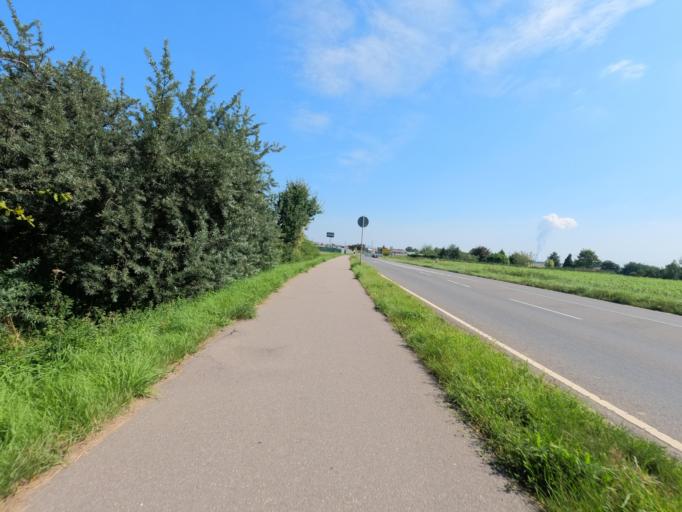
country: DE
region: North Rhine-Westphalia
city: Baesweiler
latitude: 50.9187
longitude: 6.1934
